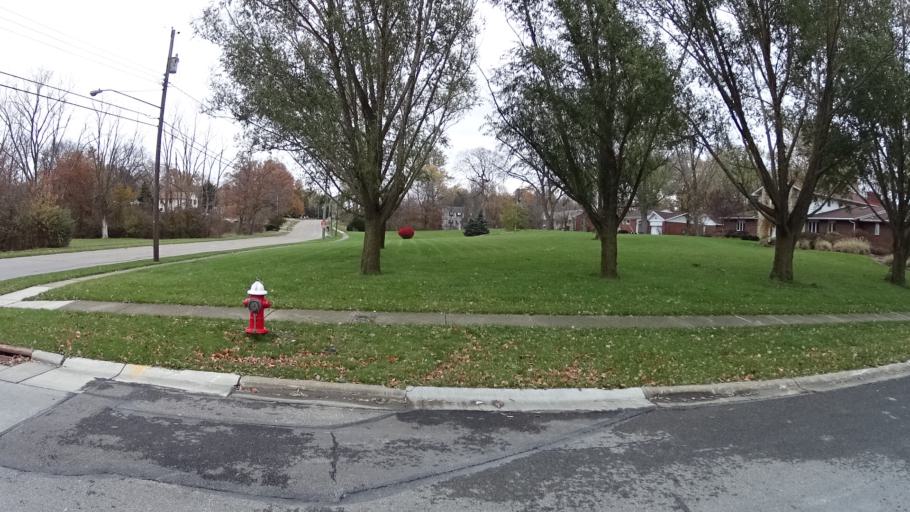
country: US
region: Ohio
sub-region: Lorain County
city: Lorain
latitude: 41.4386
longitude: -82.2081
